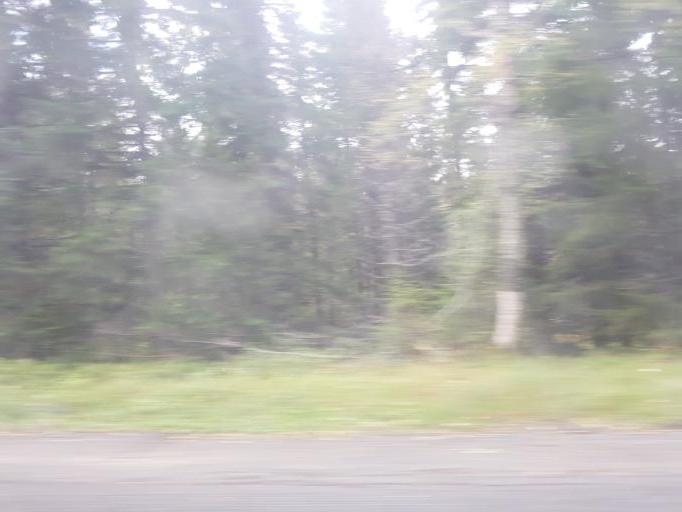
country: NO
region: Sor-Trondelag
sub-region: Trondheim
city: Trondheim
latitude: 63.4158
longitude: 10.3060
